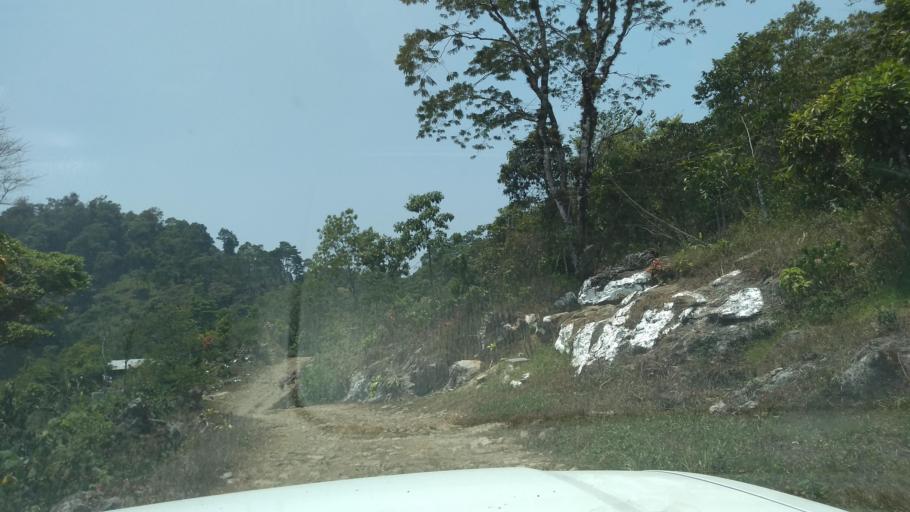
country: MX
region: Veracruz
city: Motzorongo
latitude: 18.6148
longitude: -96.7599
